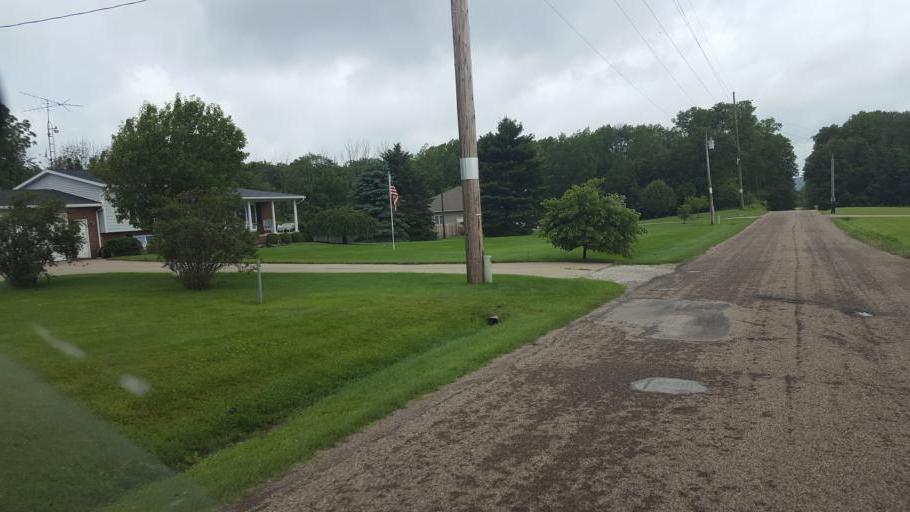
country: US
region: Ohio
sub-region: Richland County
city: Lexington
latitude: 40.6864
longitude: -82.6267
